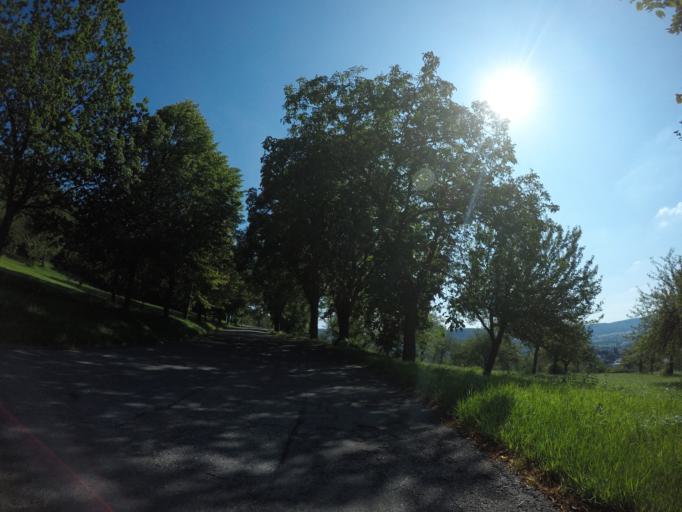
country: DE
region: Baden-Wuerttemberg
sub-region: Tuebingen Region
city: Pfullingen
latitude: 48.4671
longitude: 9.2425
